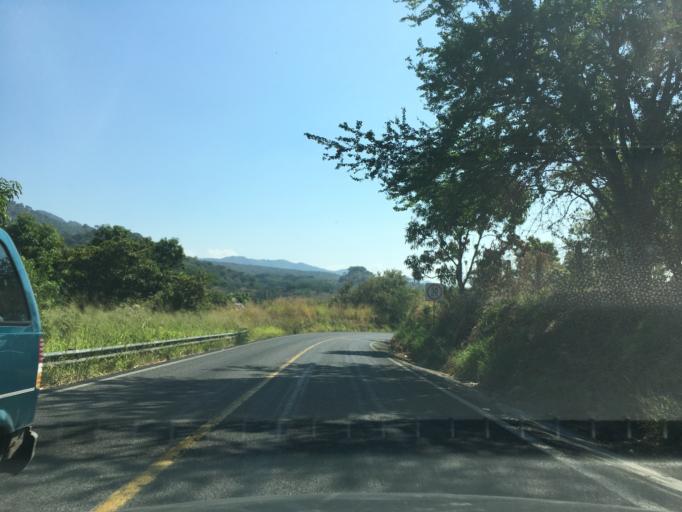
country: MX
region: Michoacan
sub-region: Gabriel Zamora
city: Lombardia
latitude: 19.2302
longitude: -102.0491
